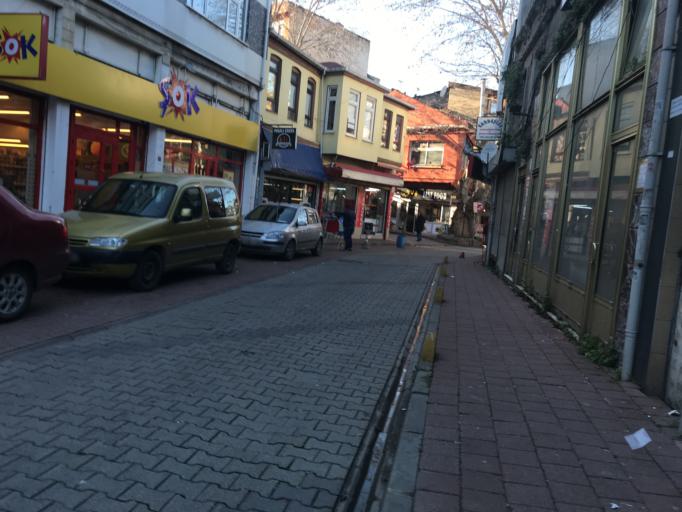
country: TR
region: Istanbul
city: Istanbul
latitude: 41.0260
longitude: 28.9563
